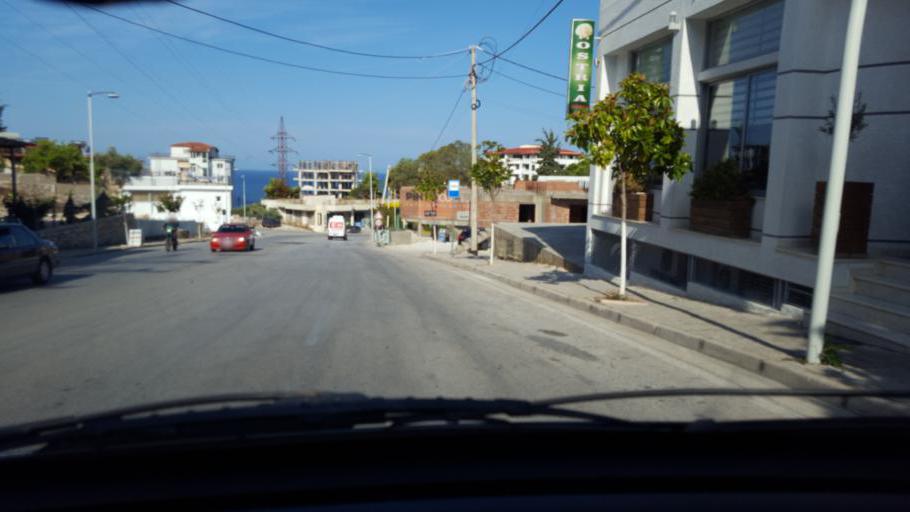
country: AL
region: Vlore
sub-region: Rrethi i Sarandes
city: Sarande
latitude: 39.8688
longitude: 20.0214
